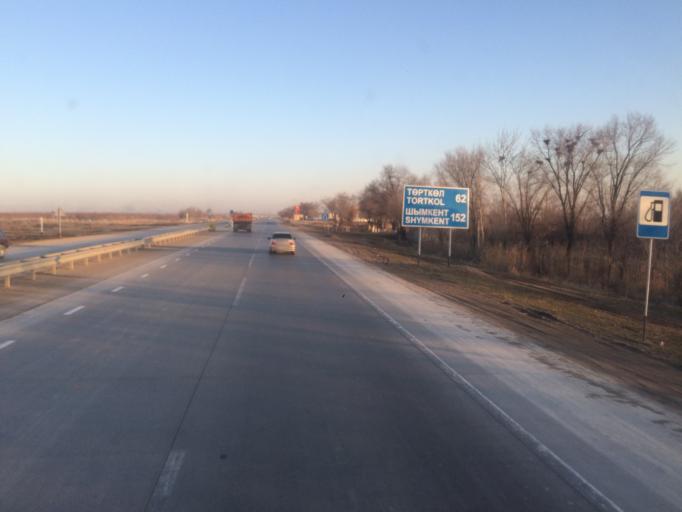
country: KZ
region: Ongtustik Qazaqstan
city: Turkestan
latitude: 43.2711
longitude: 68.3473
